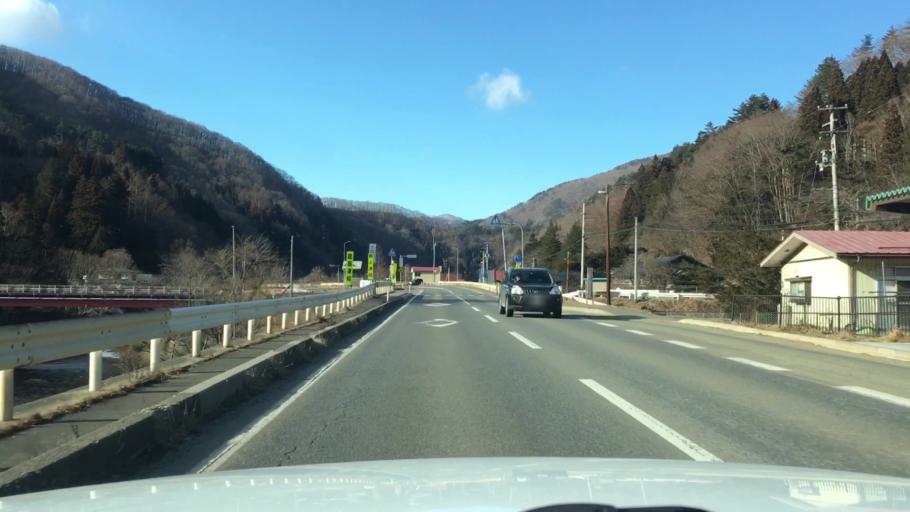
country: JP
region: Iwate
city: Tono
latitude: 39.6137
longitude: 141.6286
